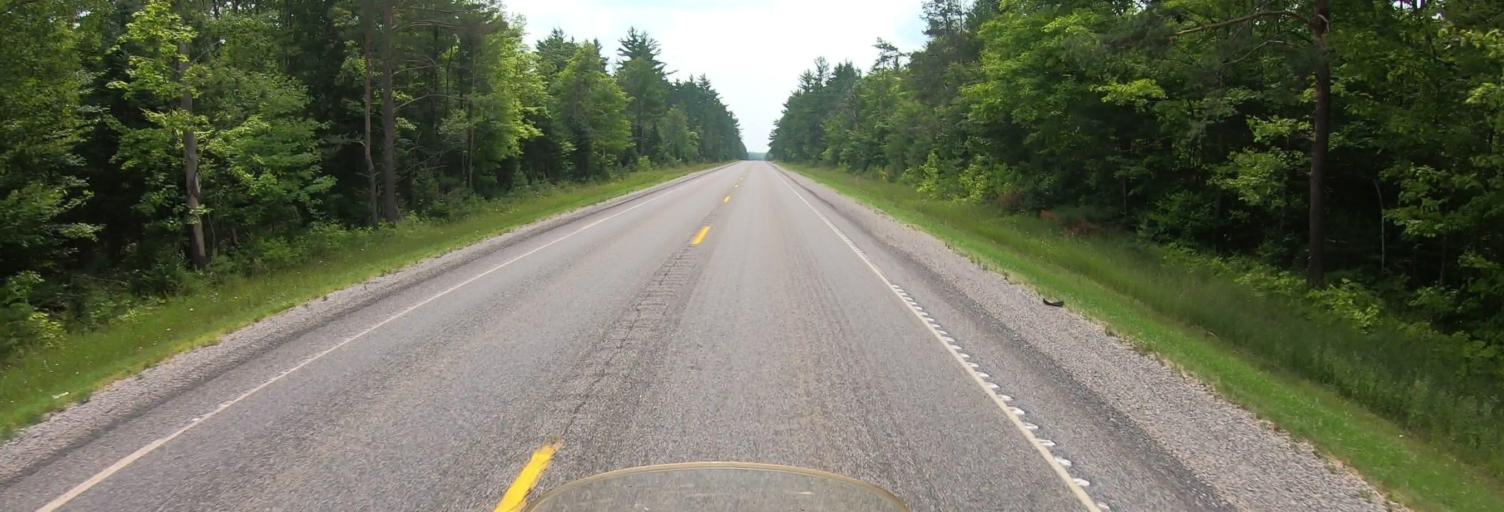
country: US
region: Michigan
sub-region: Alger County
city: Munising
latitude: 46.3492
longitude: -86.7259
